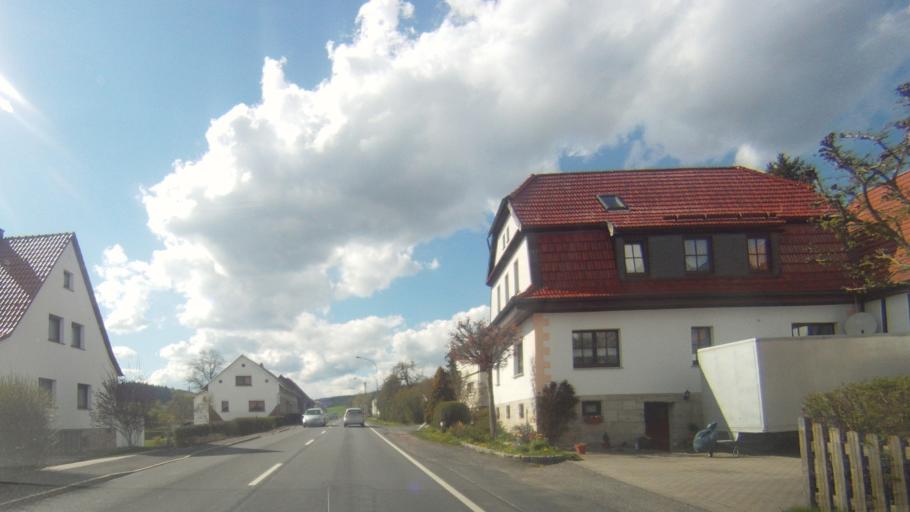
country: DE
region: Thuringia
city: Schalkau
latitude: 50.3870
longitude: 11.0565
